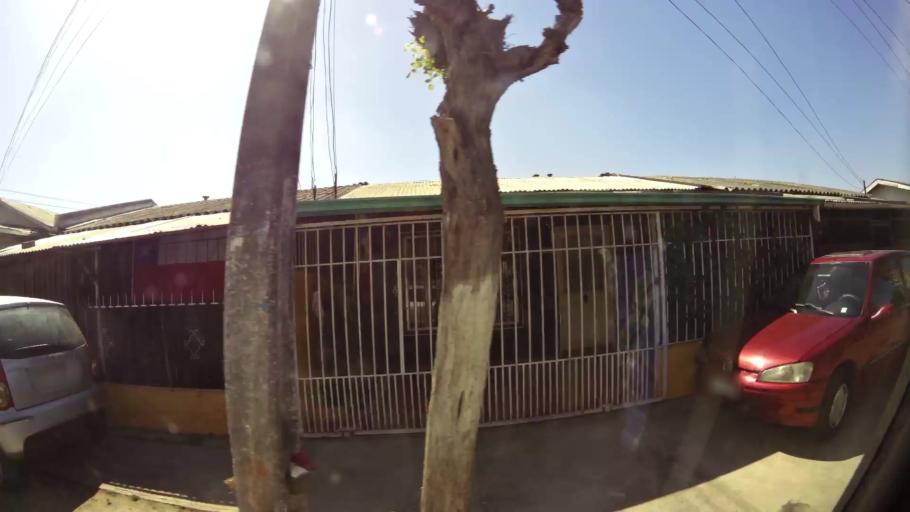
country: CL
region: Santiago Metropolitan
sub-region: Provincia de Santiago
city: Lo Prado
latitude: -33.4959
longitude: -70.7306
